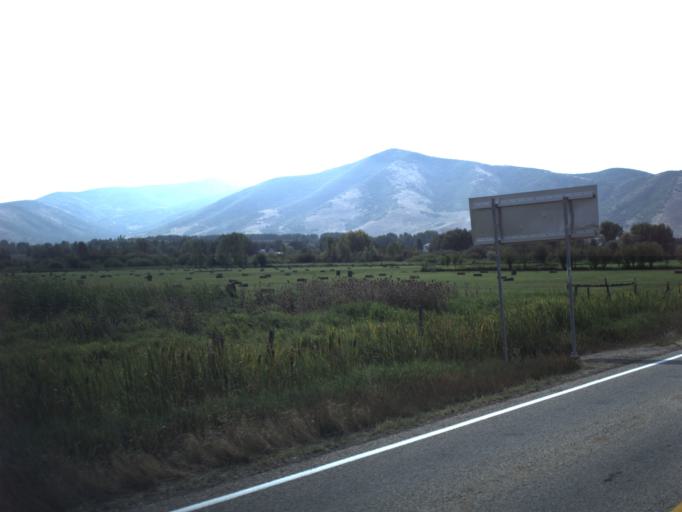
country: US
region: Utah
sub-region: Wasatch County
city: Midway
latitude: 40.4858
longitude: -111.4720
